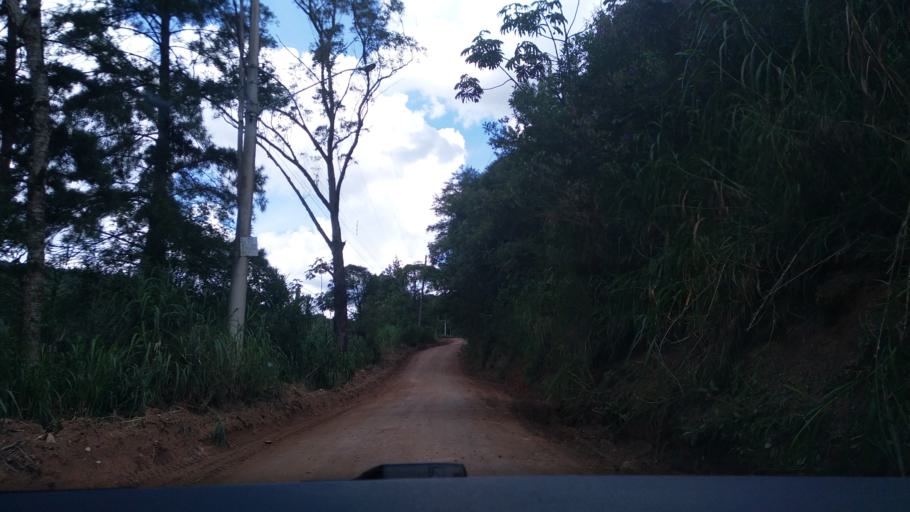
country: BR
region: Sao Paulo
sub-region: Cajamar
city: Cajamar
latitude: -23.2774
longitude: -46.8863
